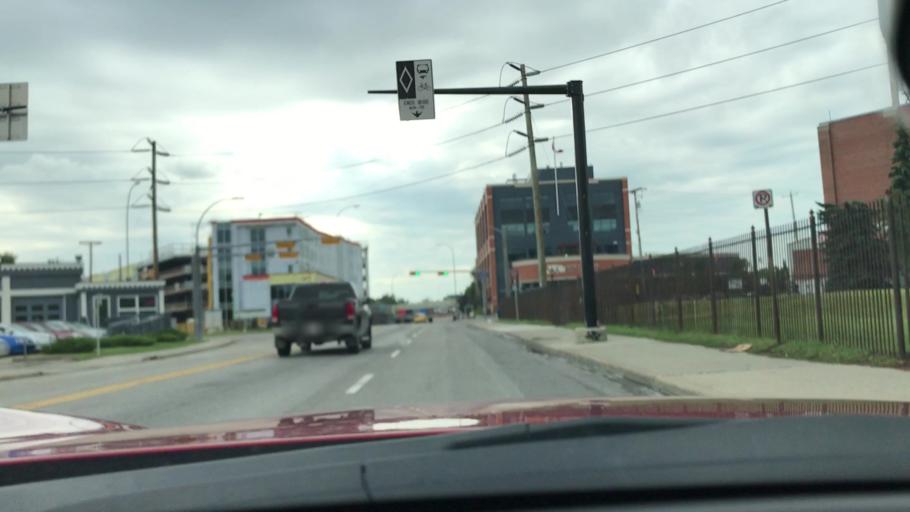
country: CA
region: Alberta
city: Calgary
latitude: 51.0381
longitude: -114.0263
